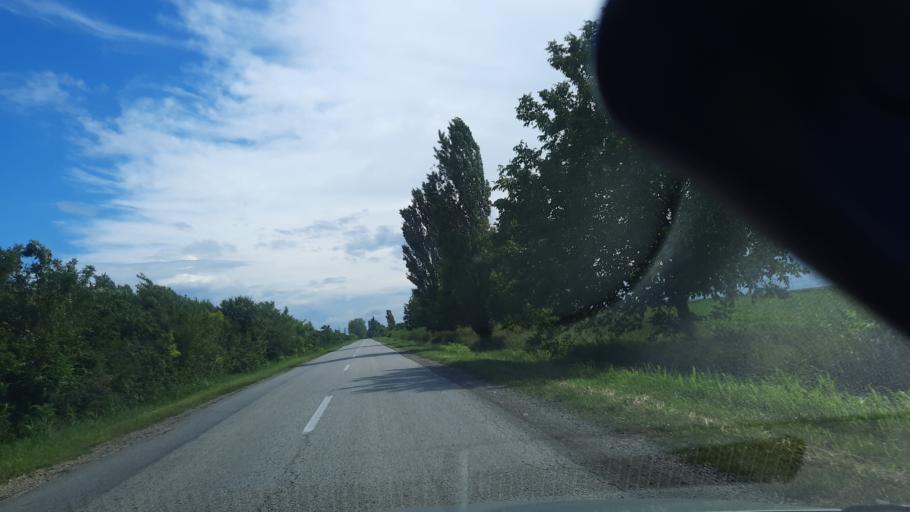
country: RS
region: Autonomna Pokrajina Vojvodina
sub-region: Sremski Okrug
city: Sremska Mitrovica
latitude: 45.0253
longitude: 19.6146
